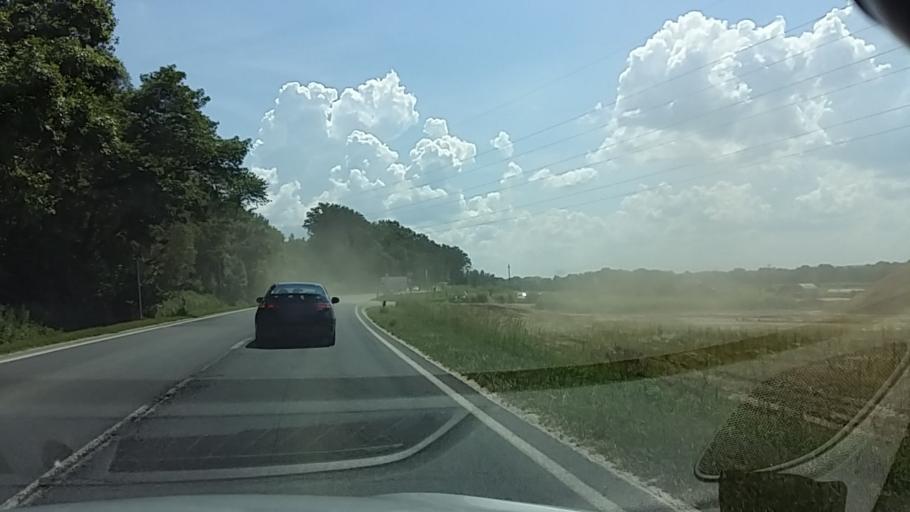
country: AT
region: Burgenland
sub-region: Politischer Bezirk Gussing
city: Heiligenbrunn
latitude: 46.9731
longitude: 16.3891
